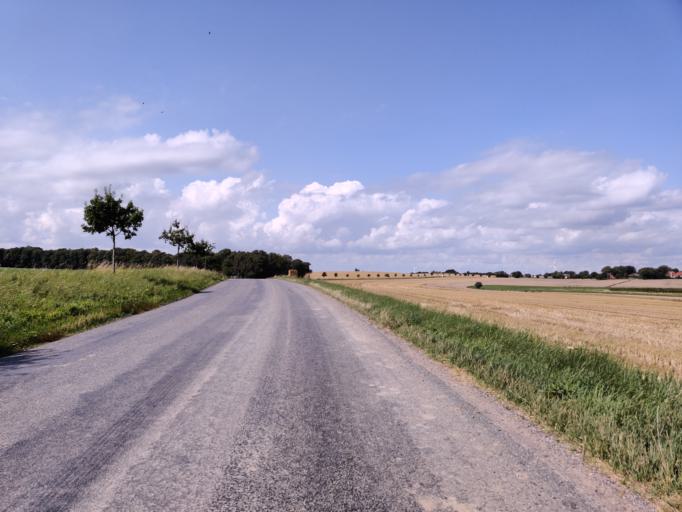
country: DK
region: Zealand
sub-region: Guldborgsund Kommune
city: Nykobing Falster
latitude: 54.6462
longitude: 11.8912
